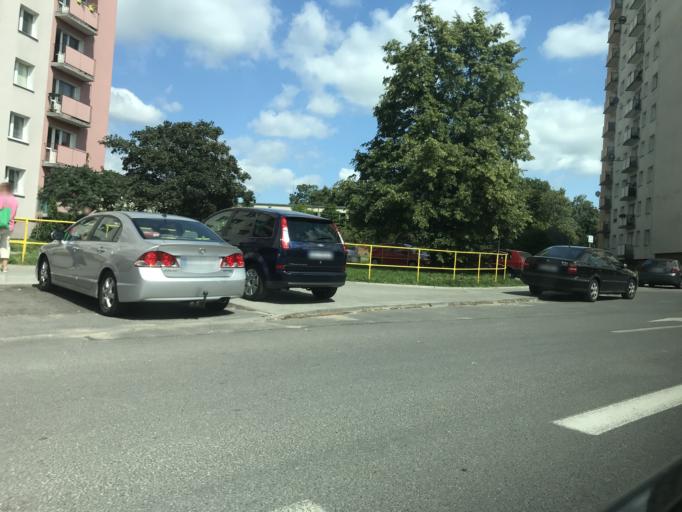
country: PL
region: Warmian-Masurian Voivodeship
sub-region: Powiat elblaski
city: Elblag
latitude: 54.1623
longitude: 19.4191
